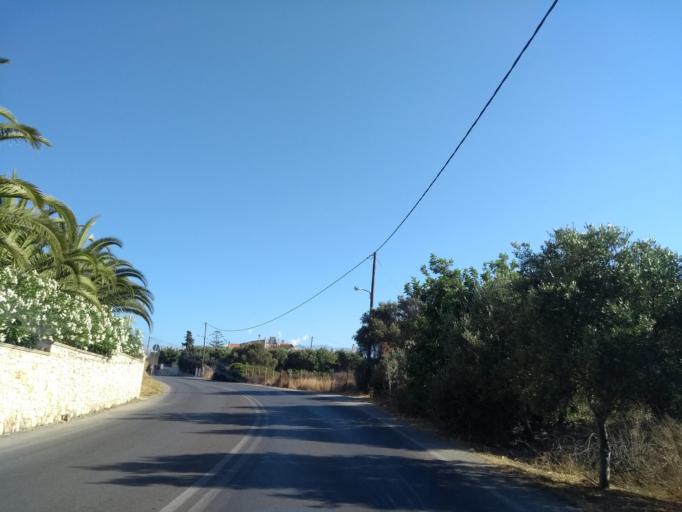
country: GR
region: Crete
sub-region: Nomos Chanias
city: Pithari
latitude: 35.5415
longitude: 24.0818
